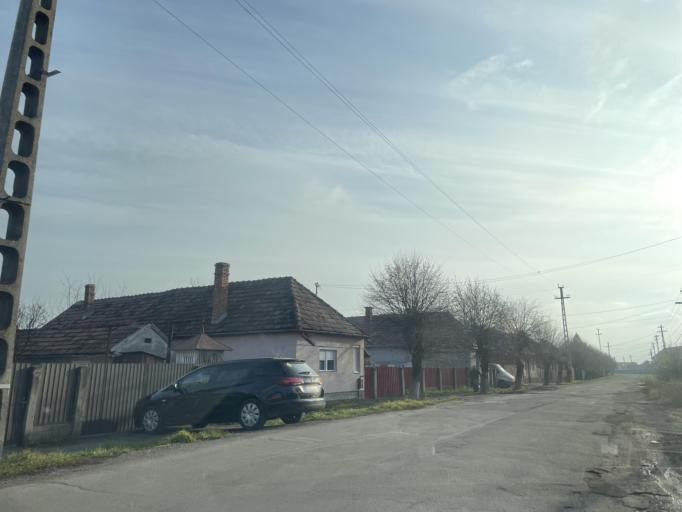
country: RO
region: Mures
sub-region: Municipiul Reghin
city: Apalina
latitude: 46.7558
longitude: 24.6942
